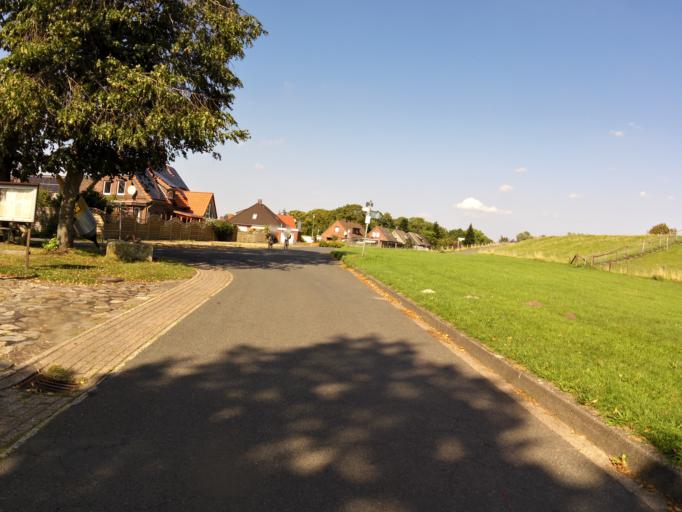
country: DE
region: Lower Saxony
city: Brake (Unterweser)
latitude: 53.4056
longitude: 8.4651
